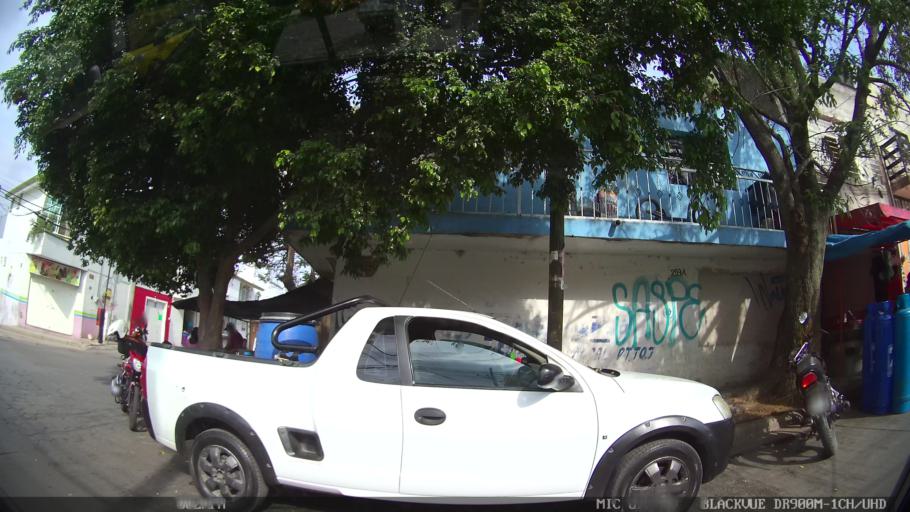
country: MX
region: Jalisco
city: Tonala
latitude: 20.6295
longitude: -103.2352
